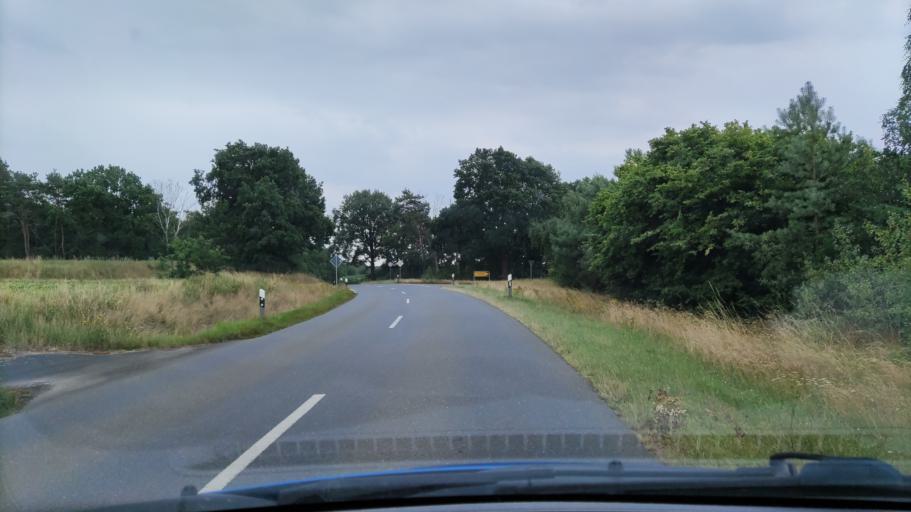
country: DE
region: Lower Saxony
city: Rosche
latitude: 53.0047
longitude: 10.7658
